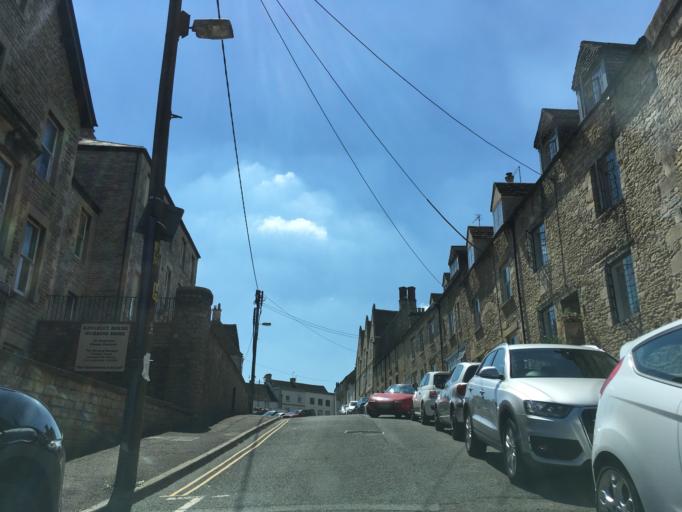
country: GB
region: England
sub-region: Gloucestershire
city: Tetbury
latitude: 51.6375
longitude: -2.1574
